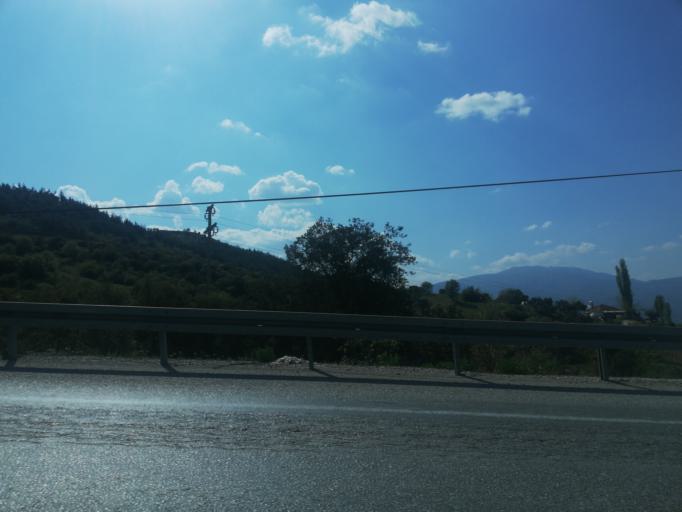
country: TR
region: Manisa
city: Sarigol
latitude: 38.1958
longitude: 28.6633
